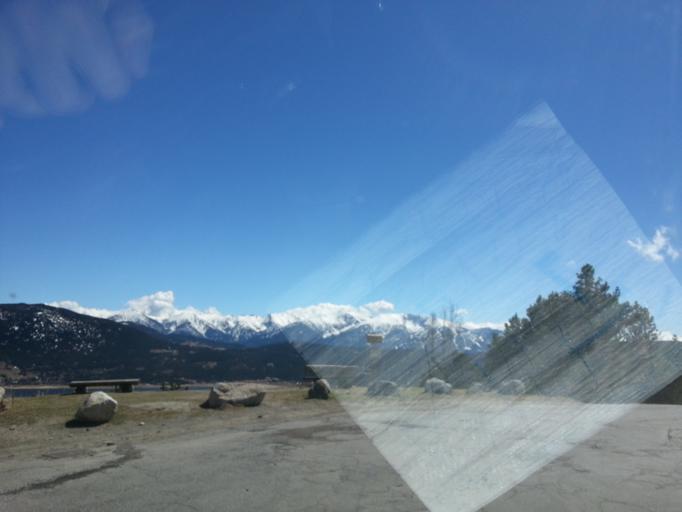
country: ES
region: Catalonia
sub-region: Provincia de Girona
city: Llivia
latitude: 42.5888
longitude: 2.0769
